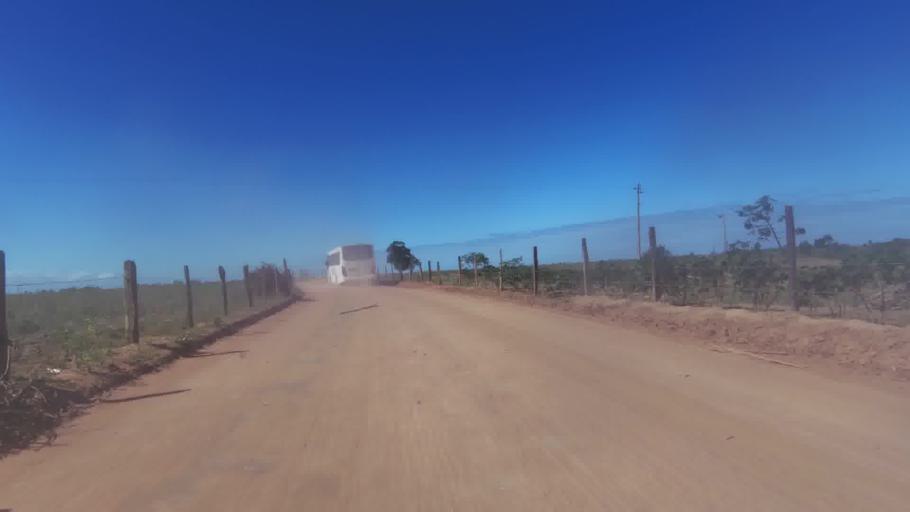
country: BR
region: Espirito Santo
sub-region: Marataizes
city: Marataizes
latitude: -21.1307
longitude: -40.9844
